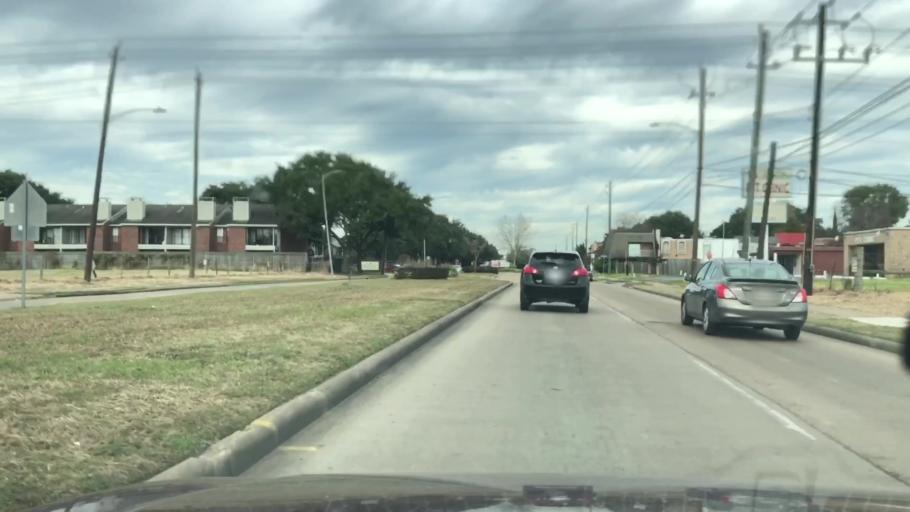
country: US
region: Texas
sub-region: Fort Bend County
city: Missouri City
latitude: 29.6666
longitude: -95.5281
